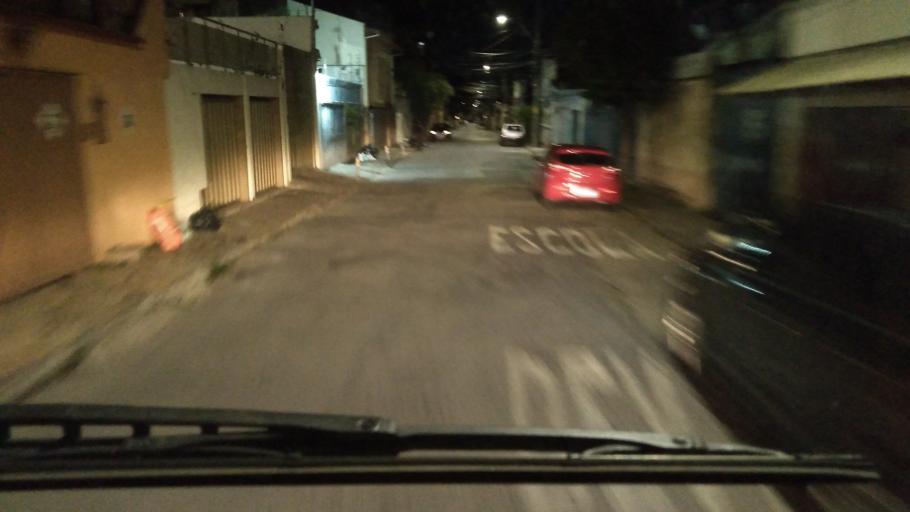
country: BR
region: Minas Gerais
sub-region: Belo Horizonte
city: Belo Horizonte
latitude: -19.9111
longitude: -43.9660
